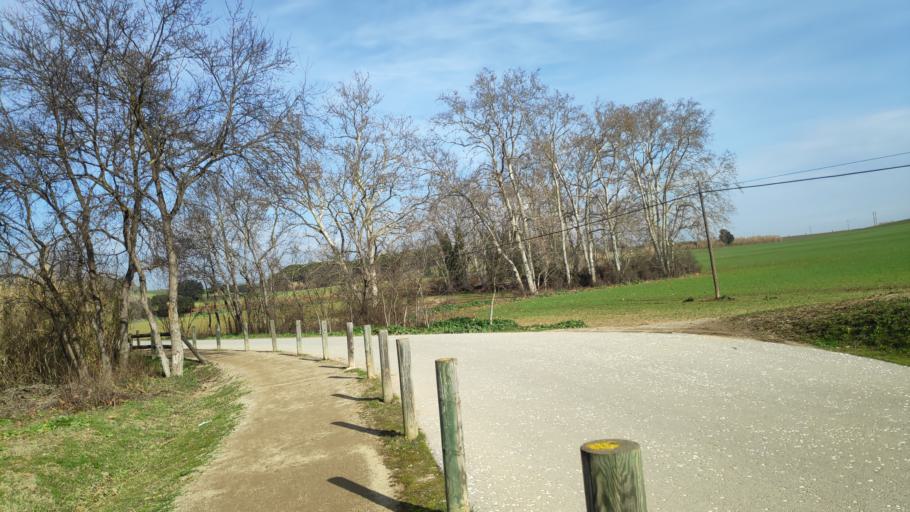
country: ES
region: Catalonia
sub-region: Provincia de Barcelona
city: Mollet del Valles
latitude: 41.5523
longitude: 2.2059
